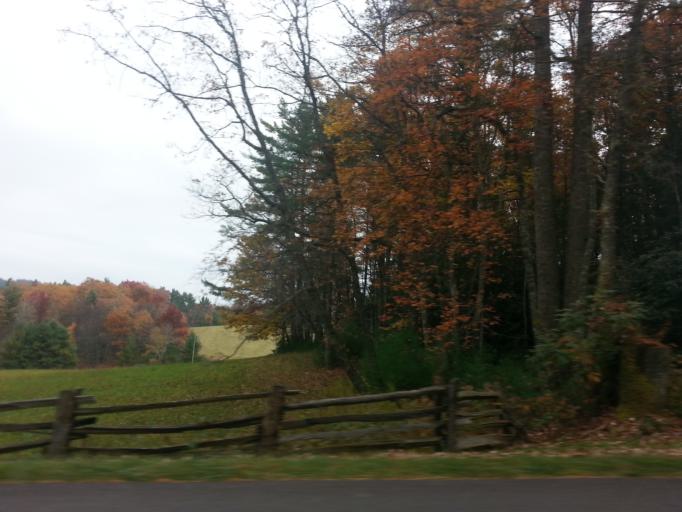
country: US
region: North Carolina
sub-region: Ashe County
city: Jefferson
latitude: 36.3516
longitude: -81.3726
